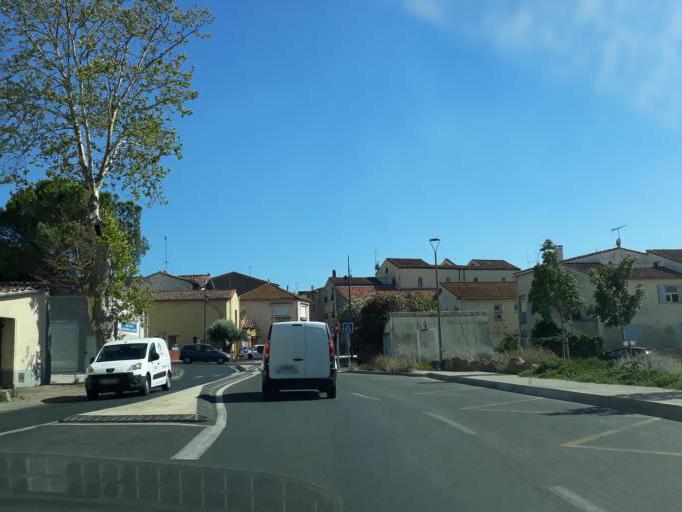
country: FR
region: Languedoc-Roussillon
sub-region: Departement de l'Herault
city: Agde
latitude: 43.3170
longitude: 3.4750
